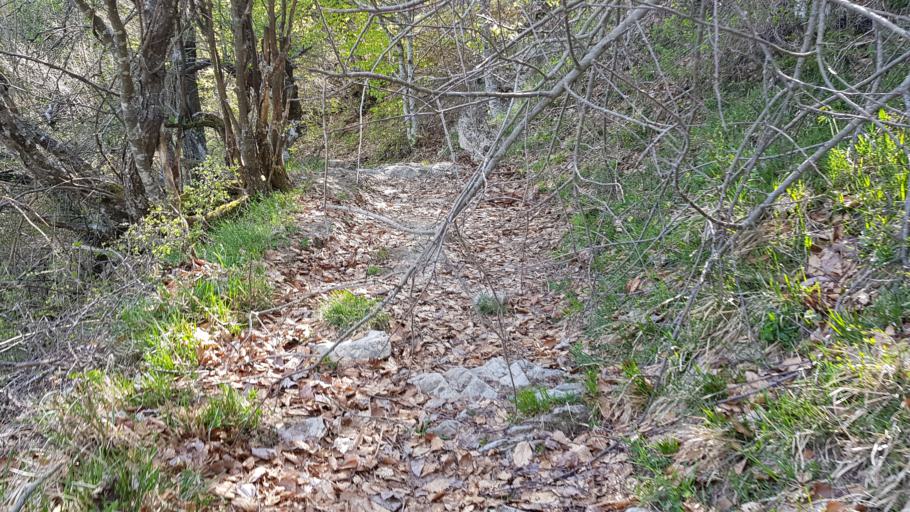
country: IT
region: Piedmont
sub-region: Provincia di Alessandria
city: Carrega Ligure
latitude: 44.6103
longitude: 9.2047
